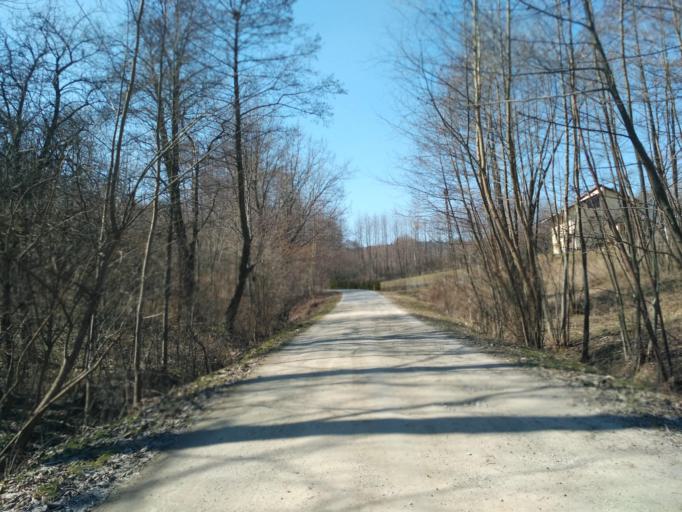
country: PL
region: Subcarpathian Voivodeship
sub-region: Powiat rzeszowski
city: Niechobrz
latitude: 49.9716
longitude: 21.8844
